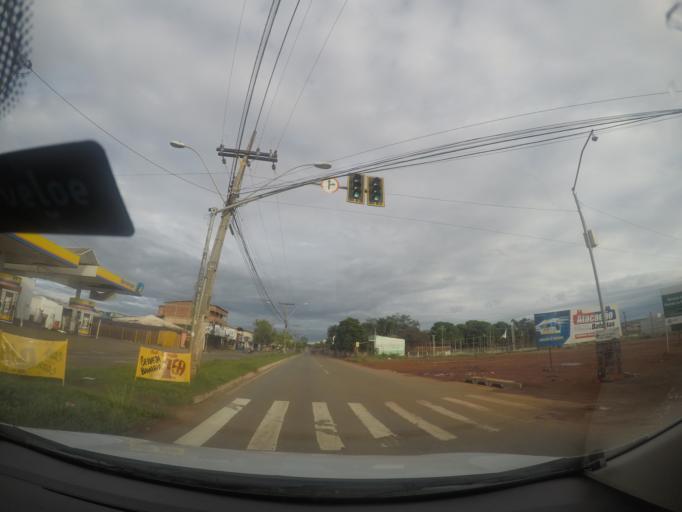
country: BR
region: Goias
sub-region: Goiania
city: Goiania
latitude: -16.6301
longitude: -49.3279
